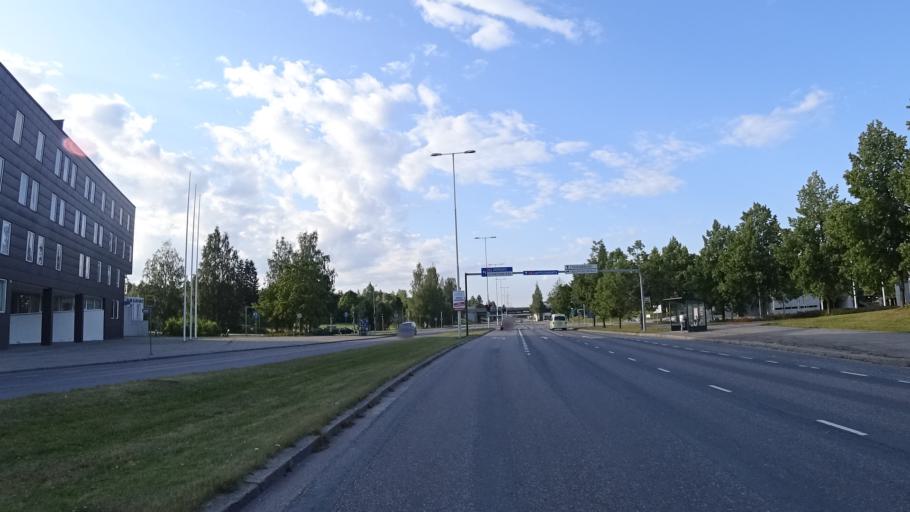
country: FI
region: South Karelia
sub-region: Imatra
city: Imatra
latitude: 61.1913
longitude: 28.7768
